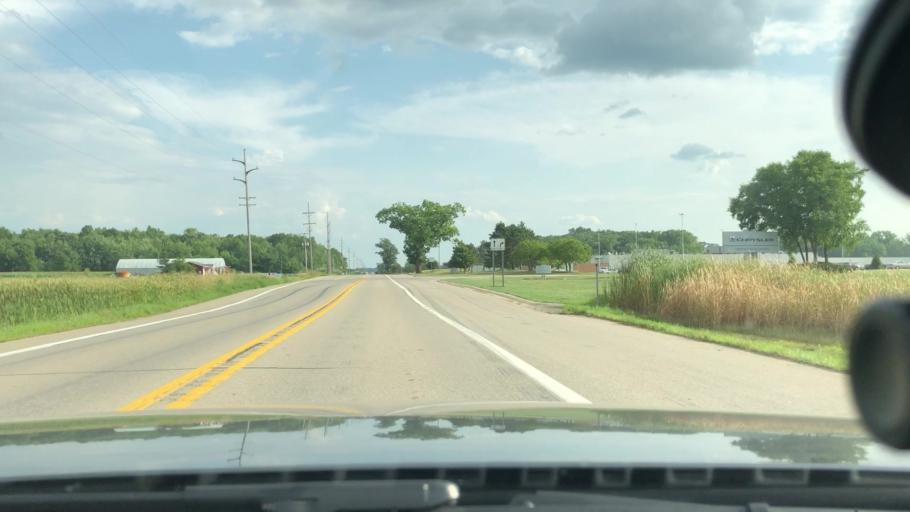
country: US
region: Michigan
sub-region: Washtenaw County
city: Chelsea
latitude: 42.2687
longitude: -84.0342
